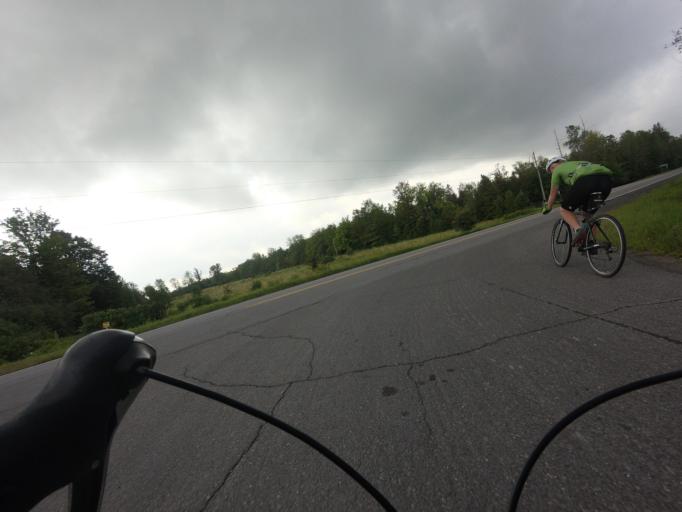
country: CA
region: Ontario
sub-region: Lanark County
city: Smiths Falls
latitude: 44.9516
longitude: -75.7851
